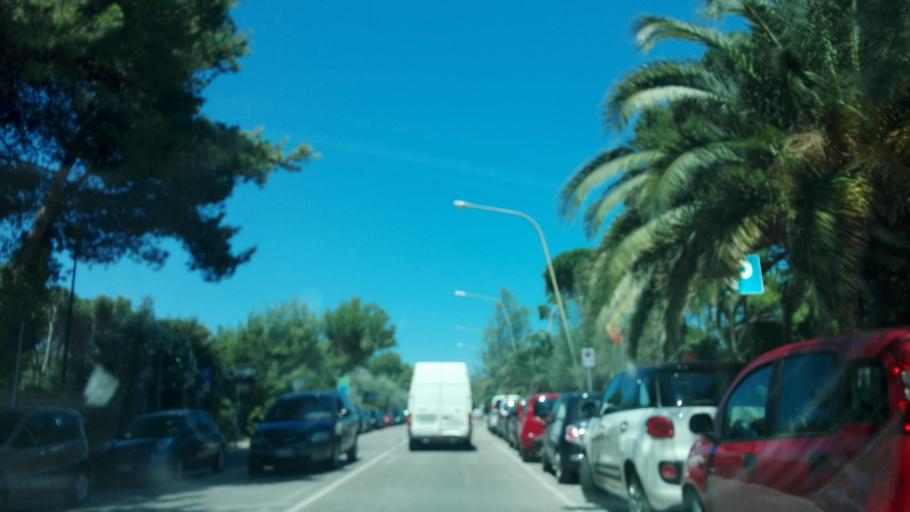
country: IT
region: Abruzzo
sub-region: Provincia di Pescara
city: Pescara
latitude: 42.4891
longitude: 14.1901
